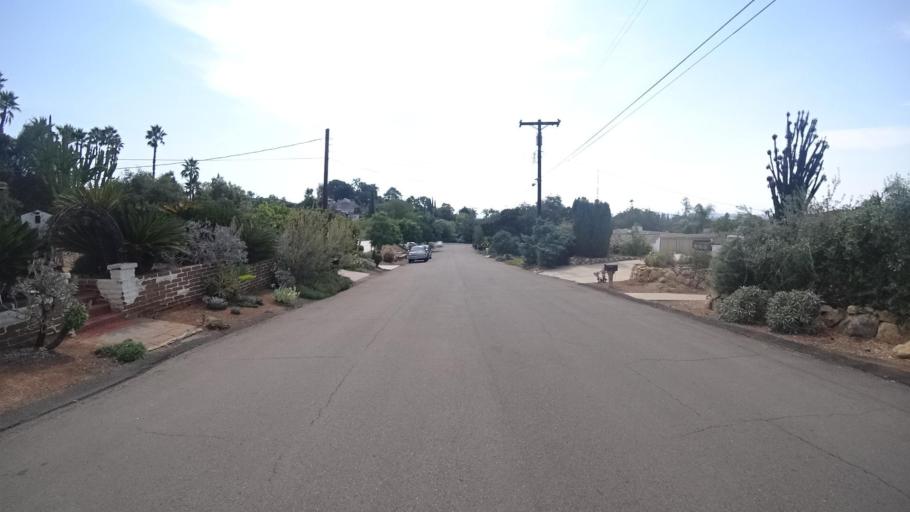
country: US
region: California
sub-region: San Diego County
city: Escondido
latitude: 33.1115
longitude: -117.0411
